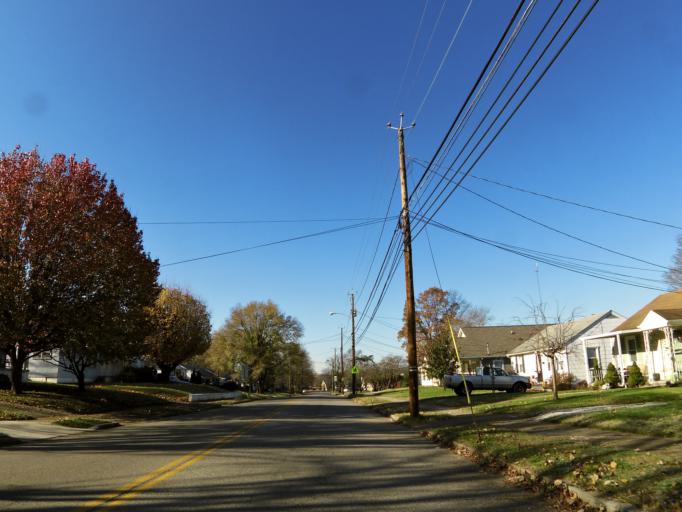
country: US
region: Tennessee
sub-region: Knox County
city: Knoxville
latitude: 35.9962
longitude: -83.9269
